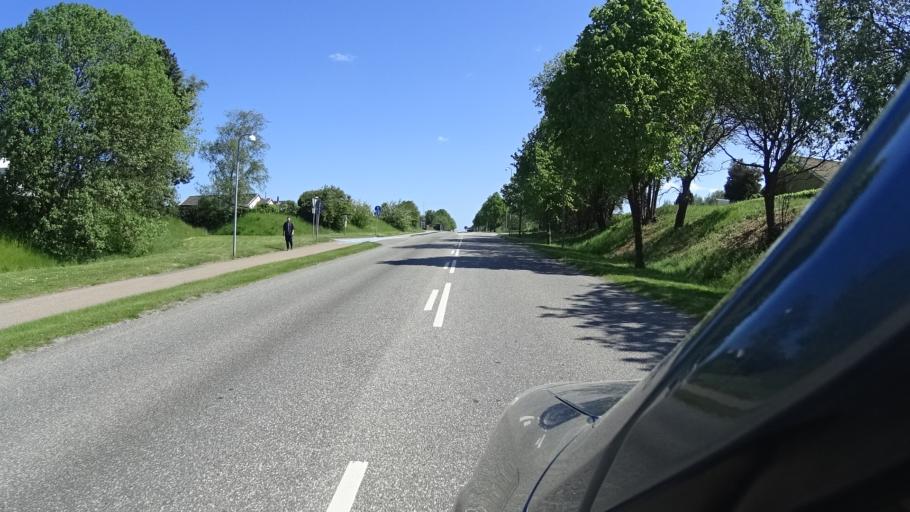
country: DK
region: South Denmark
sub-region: Vejle Kommune
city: Vejle
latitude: 55.6739
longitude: 9.5616
